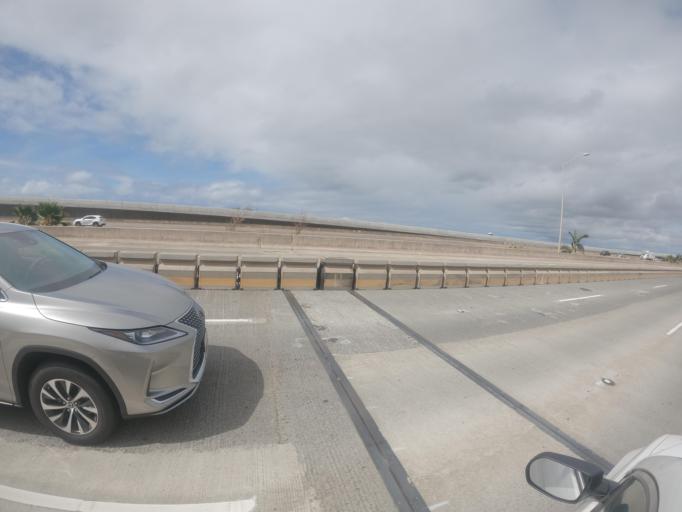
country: US
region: Hawaii
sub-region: Honolulu County
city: Hickam Field
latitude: 21.3393
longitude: -157.9271
